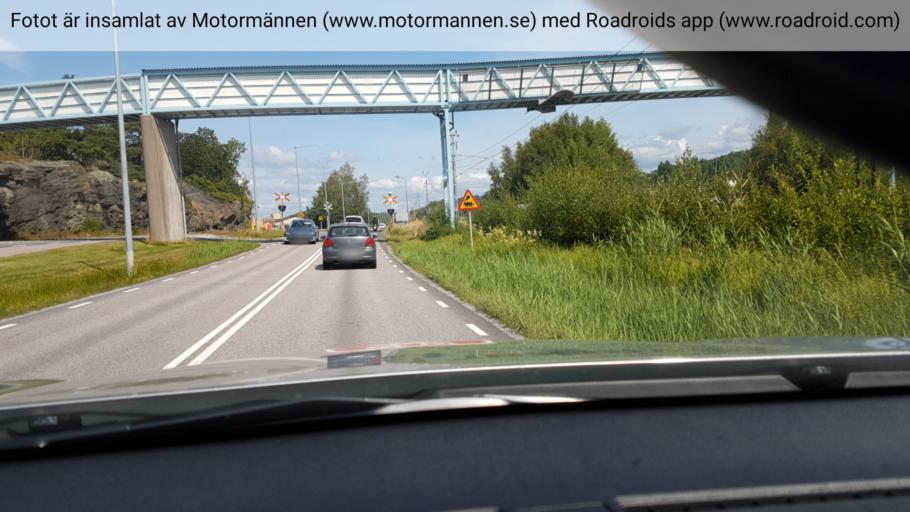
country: SE
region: Vaestra Goetaland
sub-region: Stenungsunds Kommun
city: Stenungsund
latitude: 58.0844
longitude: 11.8305
